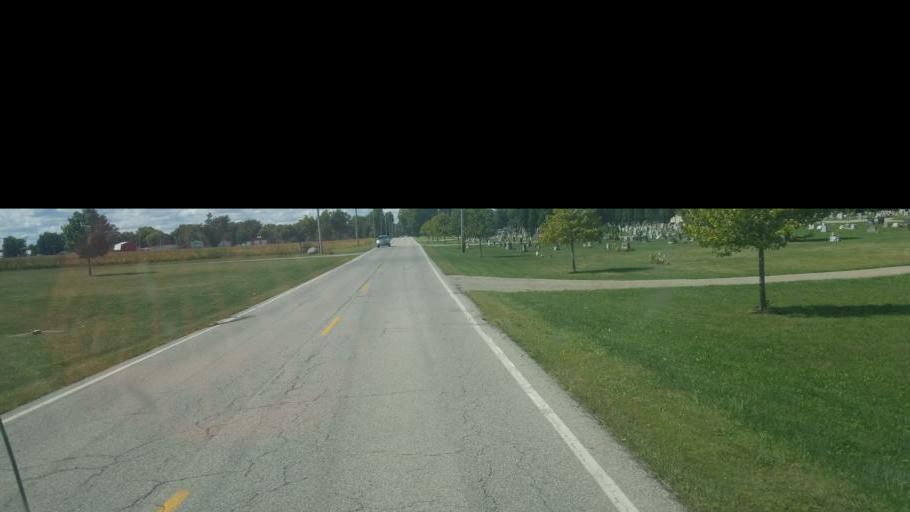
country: US
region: Ohio
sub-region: Union County
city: Marysville
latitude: 40.1758
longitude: -83.4248
